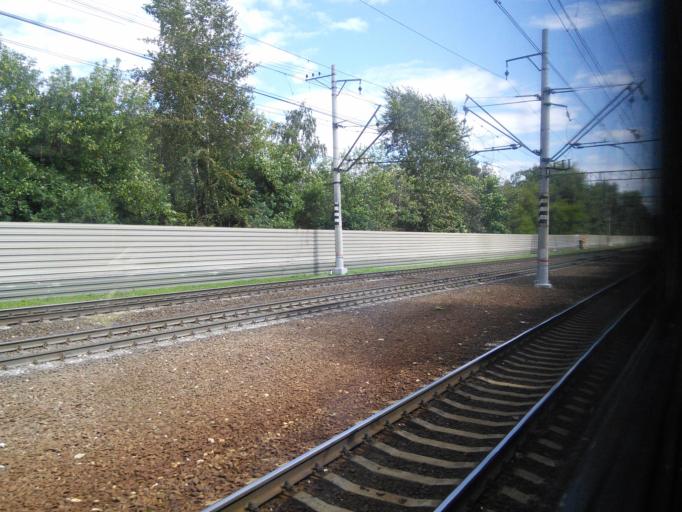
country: RU
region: Moscow
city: Zhulebino
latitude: 55.6971
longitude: 37.8674
